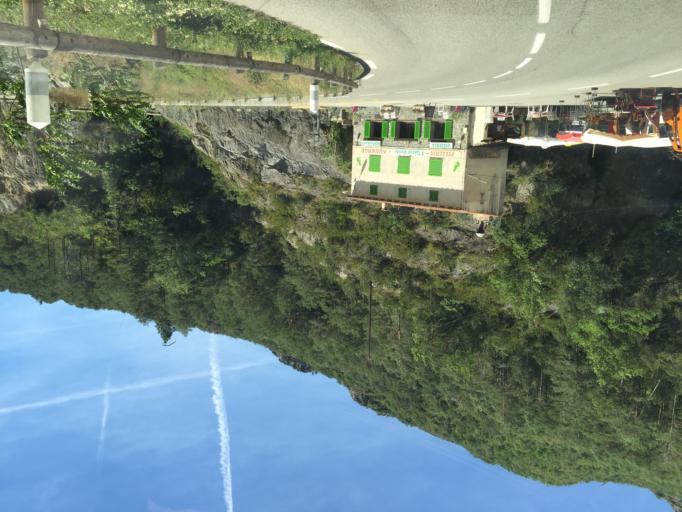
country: FR
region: Provence-Alpes-Cote d'Azur
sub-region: Departement des Alpes-Maritimes
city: Saint-Martin-Vesubie
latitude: 44.0426
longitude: 7.1286
